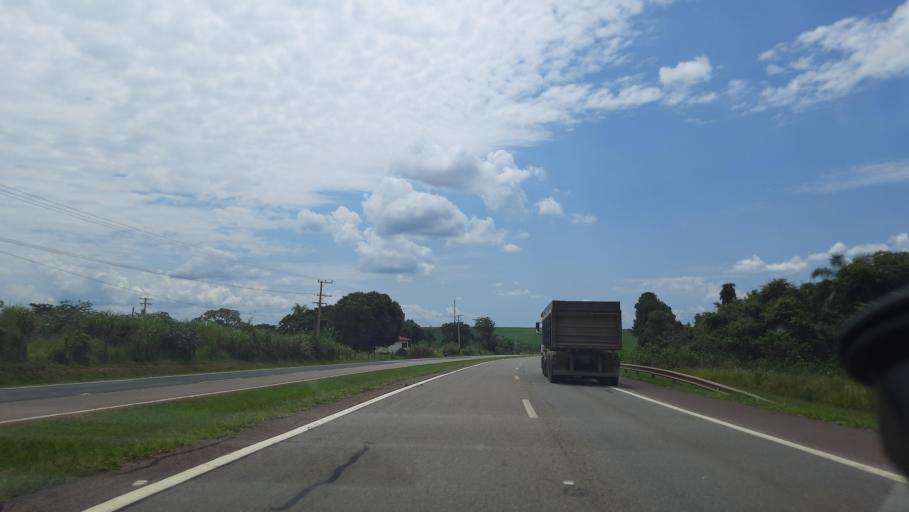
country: BR
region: Sao Paulo
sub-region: Casa Branca
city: Casa Branca
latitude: -21.7054
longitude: -47.0856
